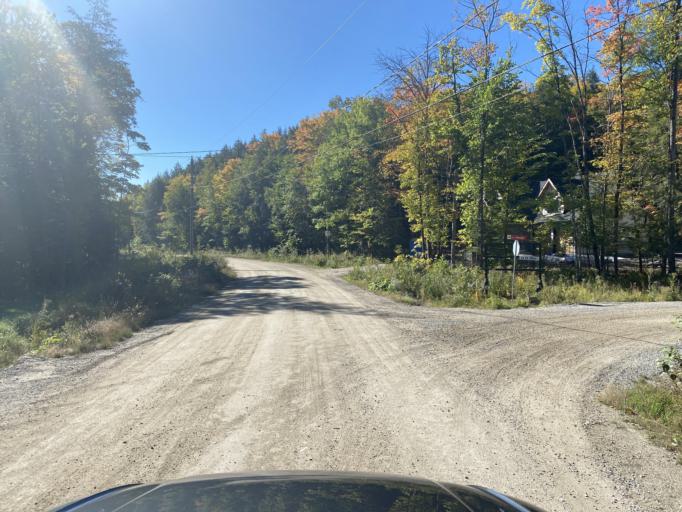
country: CA
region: Quebec
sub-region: Outaouais
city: Wakefield
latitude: 45.6378
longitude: -75.9071
